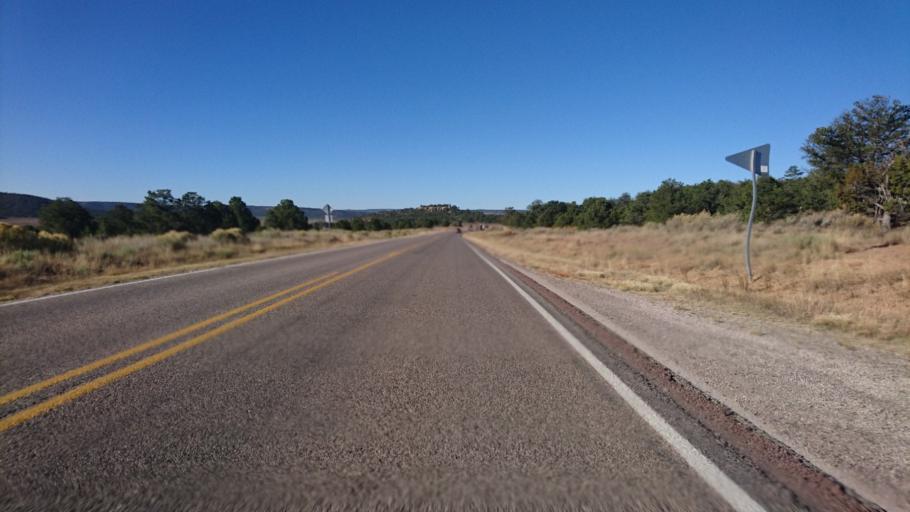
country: US
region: New Mexico
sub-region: McKinley County
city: Black Rock
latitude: 35.1279
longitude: -108.5284
